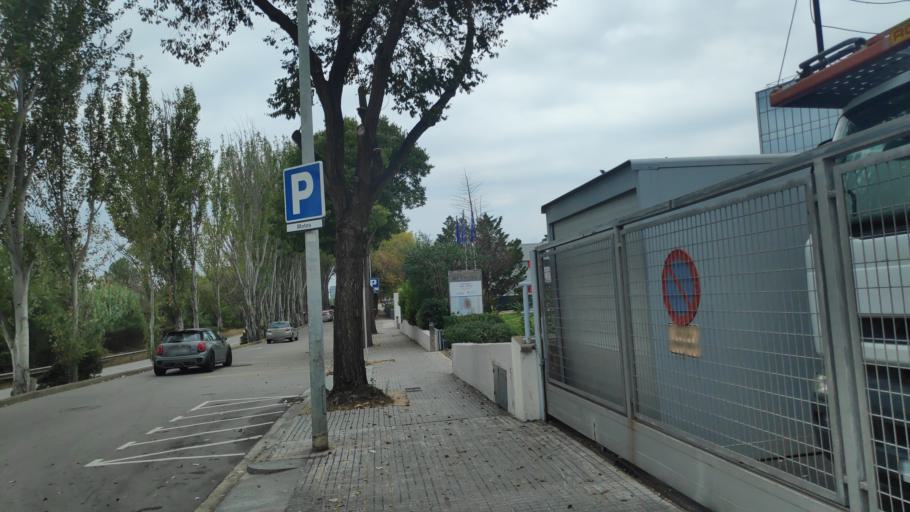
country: ES
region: Catalonia
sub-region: Provincia de Barcelona
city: Sant Cugat del Valles
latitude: 41.4797
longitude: 2.0620
